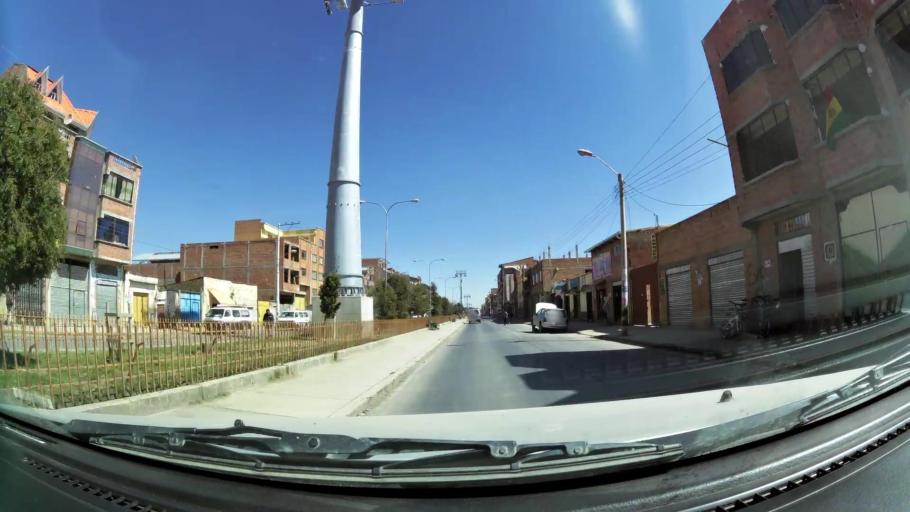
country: BO
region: La Paz
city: La Paz
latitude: -16.4912
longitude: -68.1869
